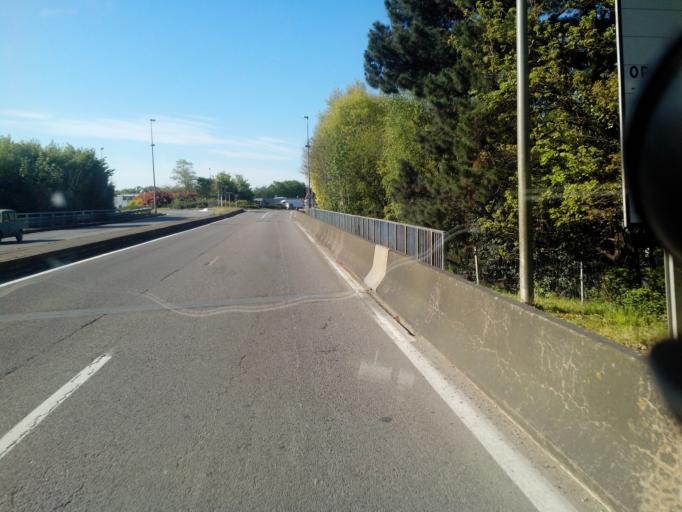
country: FR
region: Pays de la Loire
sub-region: Departement de la Loire-Atlantique
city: Orvault
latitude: 47.2596
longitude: -1.6241
